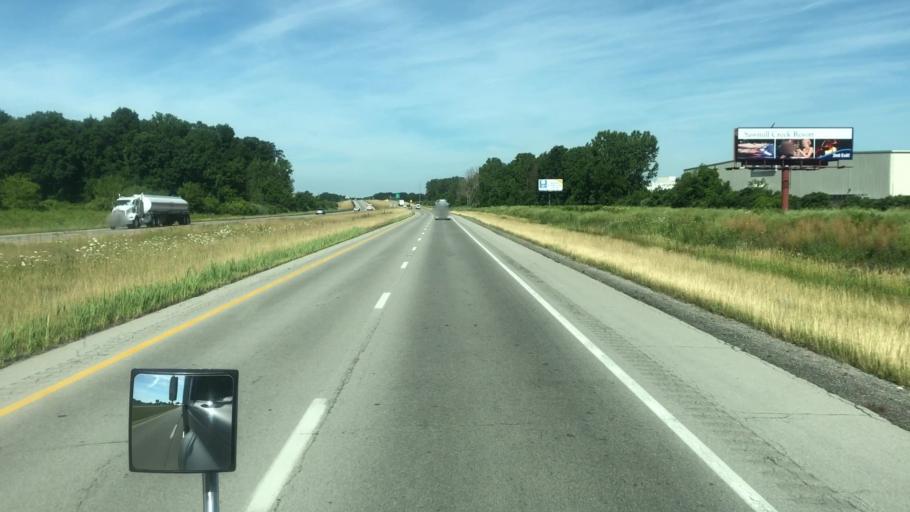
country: US
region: Ohio
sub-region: Erie County
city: Huron
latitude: 41.3694
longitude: -82.5334
